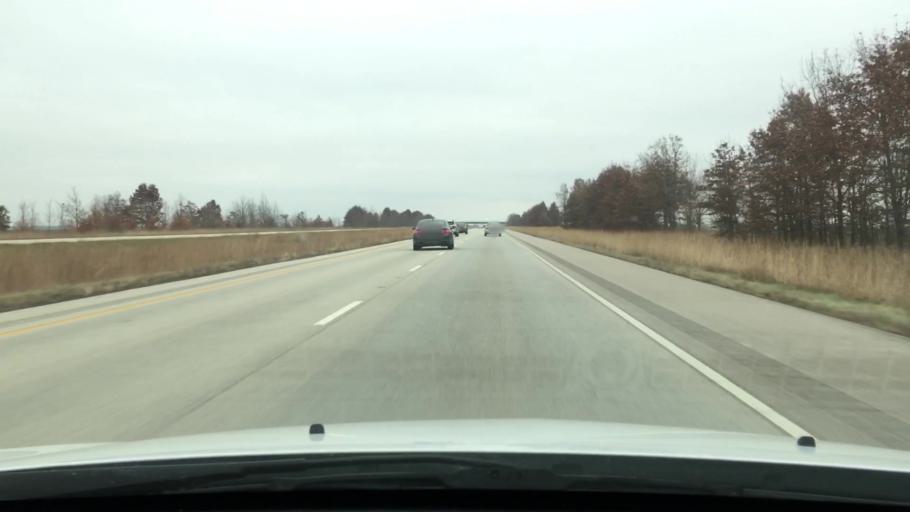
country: US
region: Illinois
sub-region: Sangamon County
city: New Berlin
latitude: 39.7407
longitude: -89.8559
